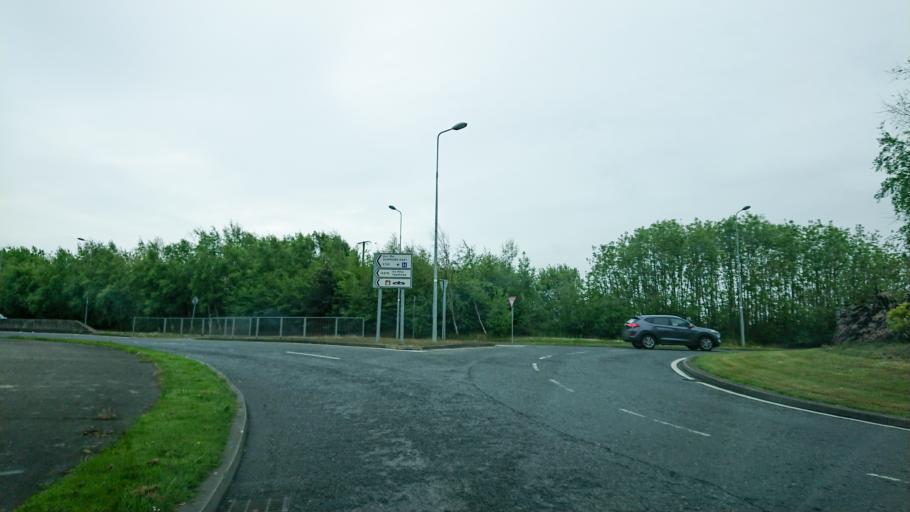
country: IE
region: Munster
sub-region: Waterford
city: Waterford
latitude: 52.2312
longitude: -7.1432
